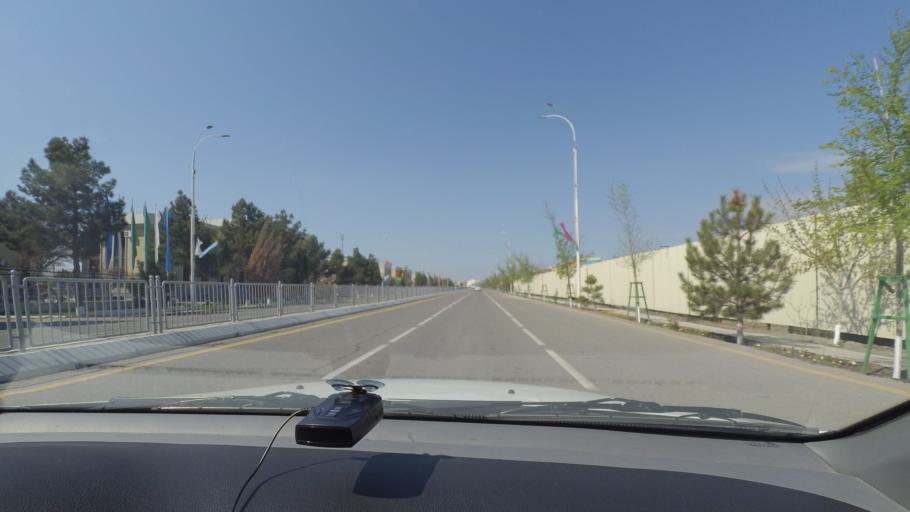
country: UZ
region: Bukhara
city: Bukhara
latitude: 39.7673
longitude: 64.4695
